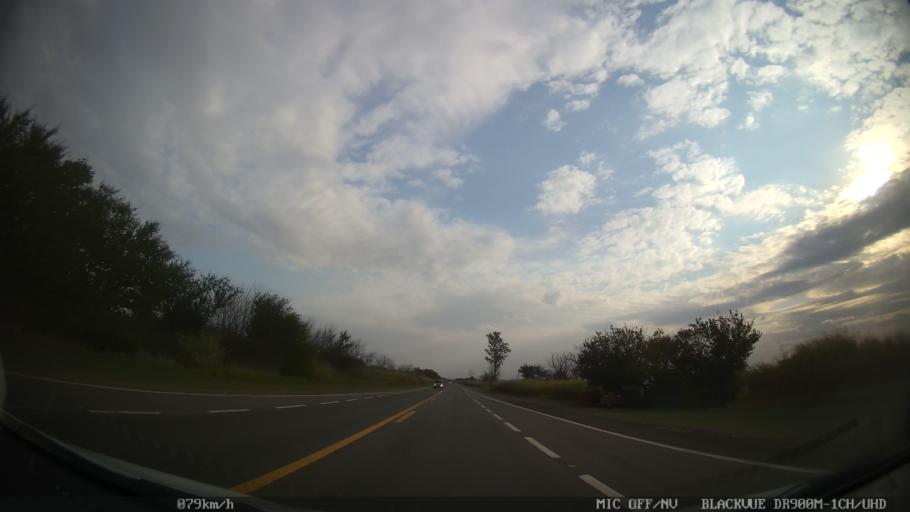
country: BR
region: Sao Paulo
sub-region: Cosmopolis
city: Cosmopolis
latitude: -22.6139
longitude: -47.2395
